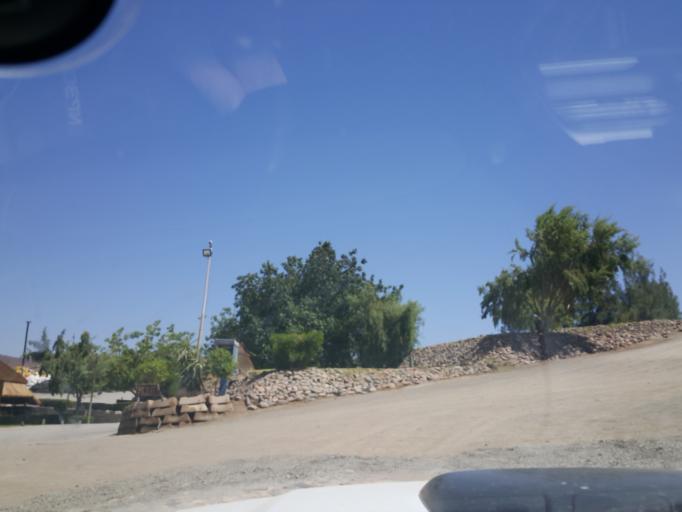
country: ZA
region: Northern Cape
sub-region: Namakwa District Municipality
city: Port Nolloth
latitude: -28.6864
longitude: 17.5579
